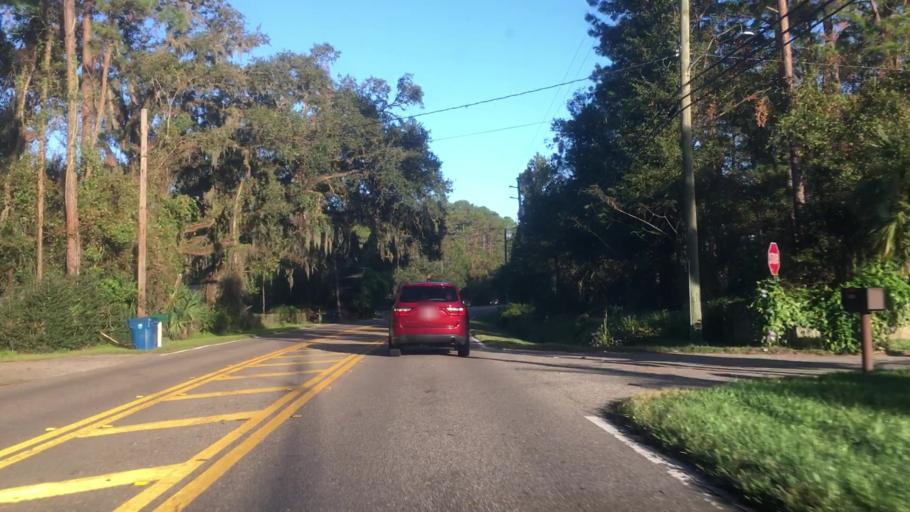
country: US
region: Florida
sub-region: Duval County
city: Jacksonville
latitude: 30.4662
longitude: -81.5971
